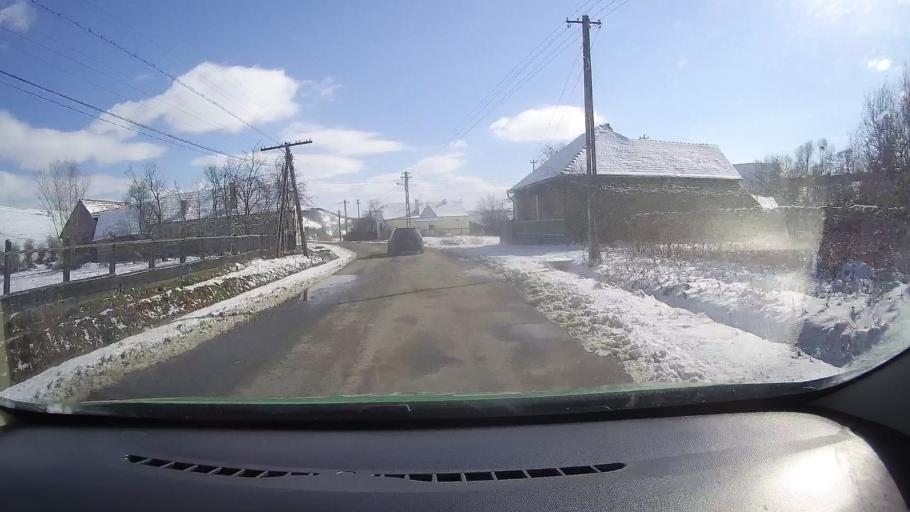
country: RO
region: Sibiu
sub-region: Comuna Altina
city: Altina
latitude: 45.9820
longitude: 24.4576
